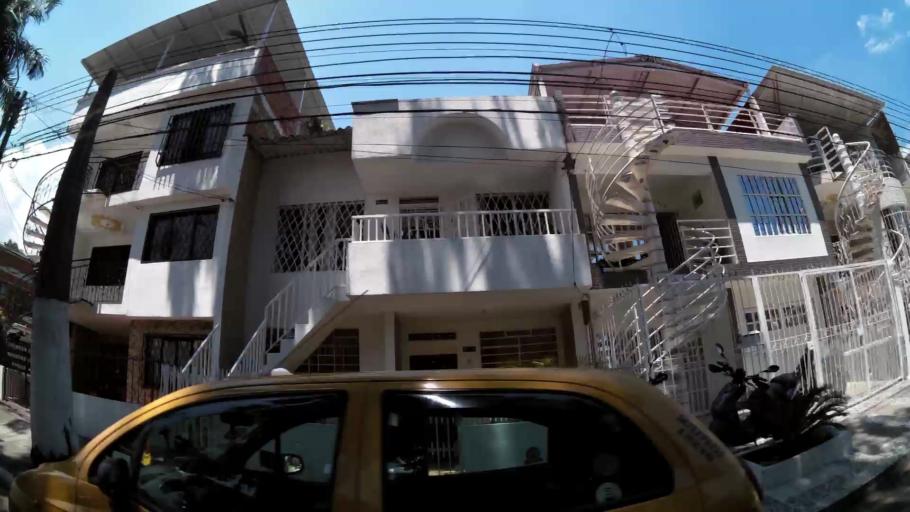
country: CO
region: Valle del Cauca
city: Cali
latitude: 3.4508
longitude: -76.4969
